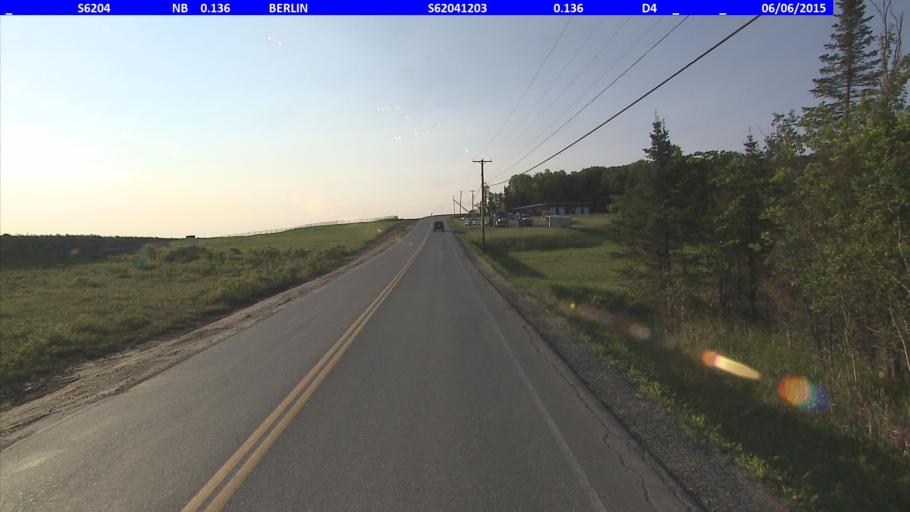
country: US
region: Vermont
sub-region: Washington County
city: South Barre
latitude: 44.1947
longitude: -72.5568
